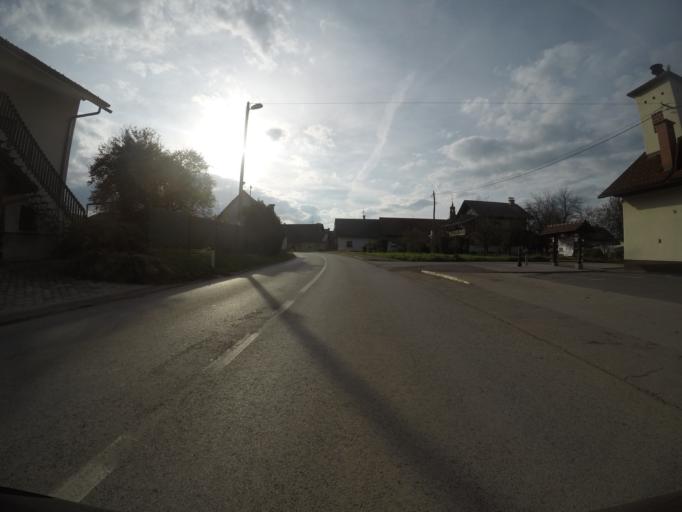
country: SI
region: Vodice
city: Vodice
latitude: 46.1803
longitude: 14.4694
